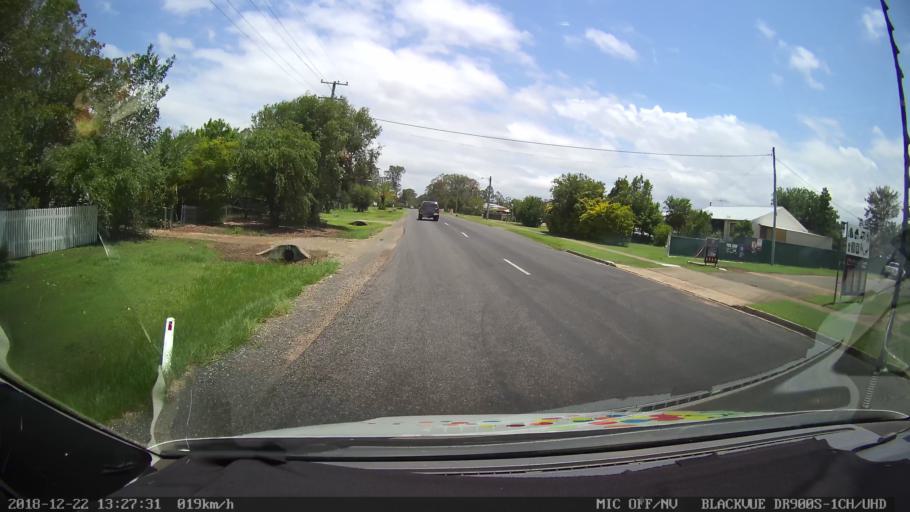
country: AU
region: New South Wales
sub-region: Clarence Valley
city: Coutts Crossing
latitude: -29.8283
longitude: 152.8917
